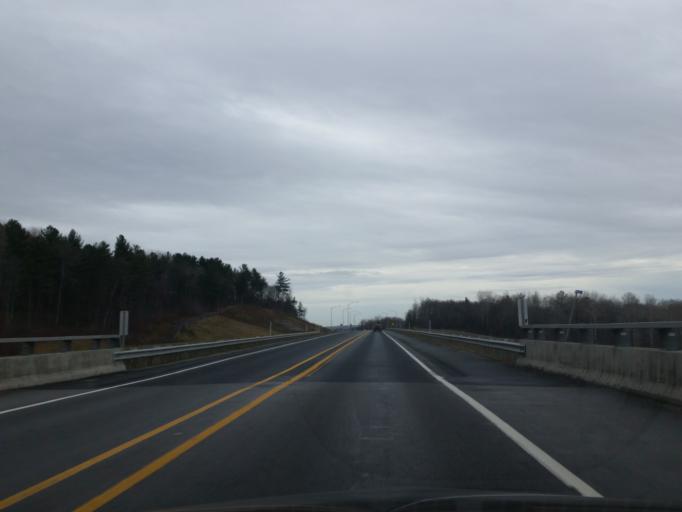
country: CA
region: Quebec
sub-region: Outaouais
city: Papineauville
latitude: 45.6586
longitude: -74.8689
